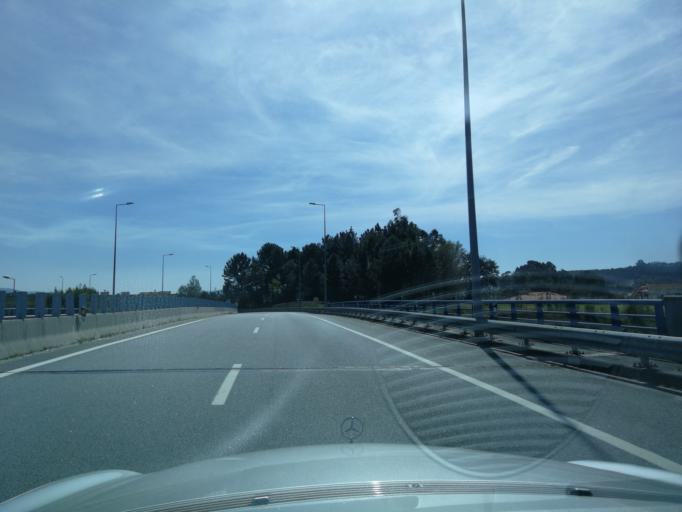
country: PT
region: Braga
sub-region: Vila Nova de Famalicao
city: Calendario
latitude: 41.3860
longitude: -8.5178
